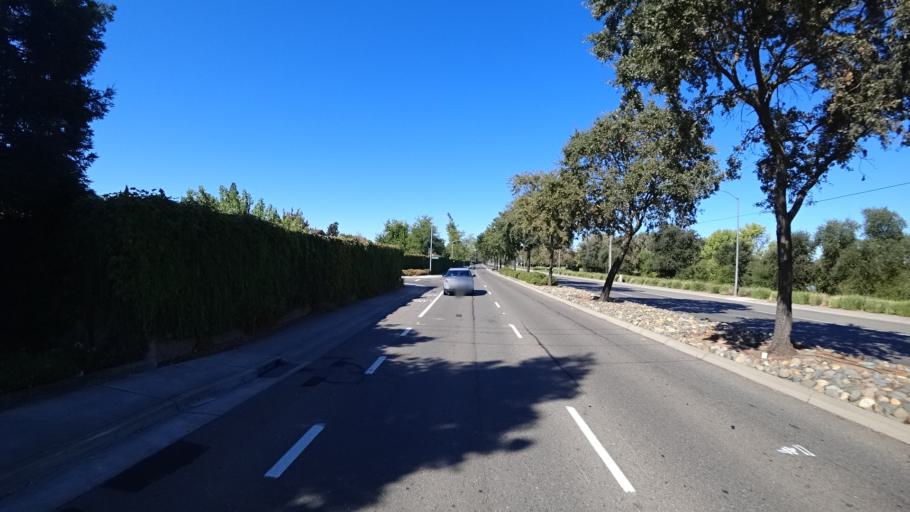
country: US
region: California
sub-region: Sacramento County
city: Elk Grove
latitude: 38.4235
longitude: -121.3763
